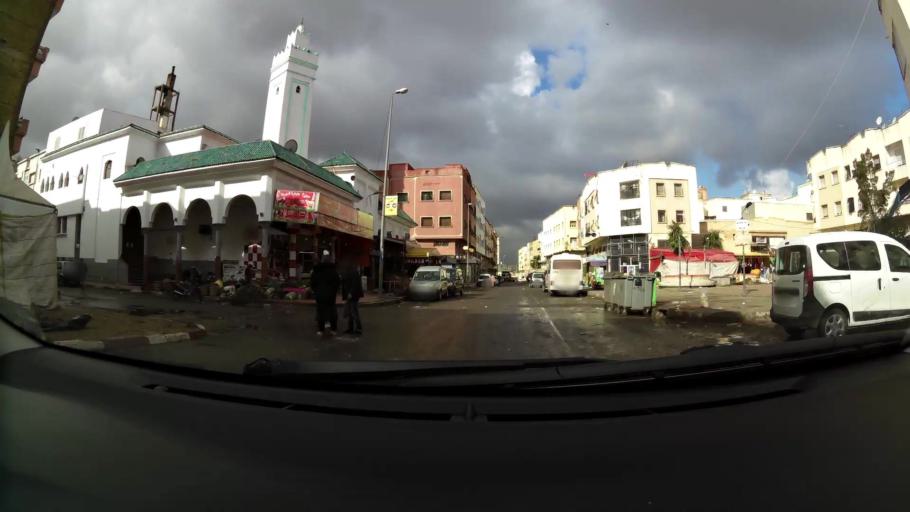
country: MA
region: Grand Casablanca
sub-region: Mediouna
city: Tit Mellil
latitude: 33.5929
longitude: -7.5186
